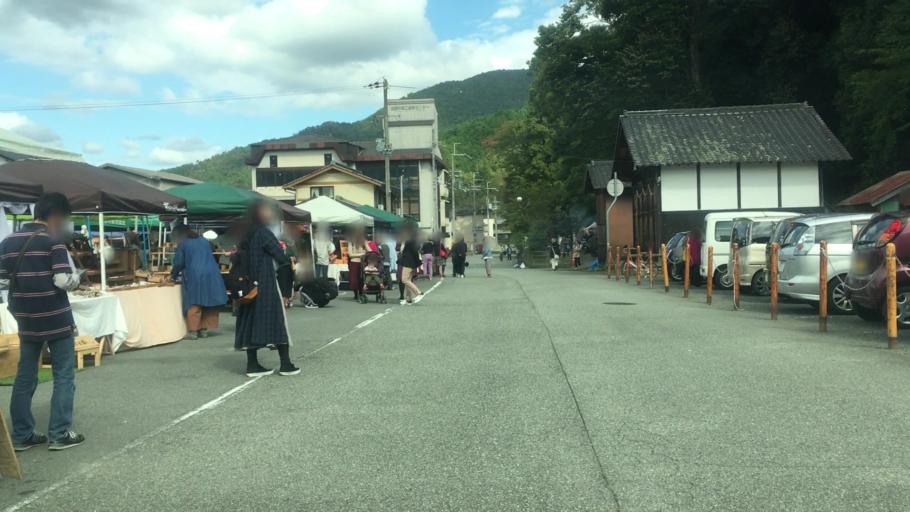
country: JP
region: Hyogo
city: Sasayama
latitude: 35.1305
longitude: 135.0784
